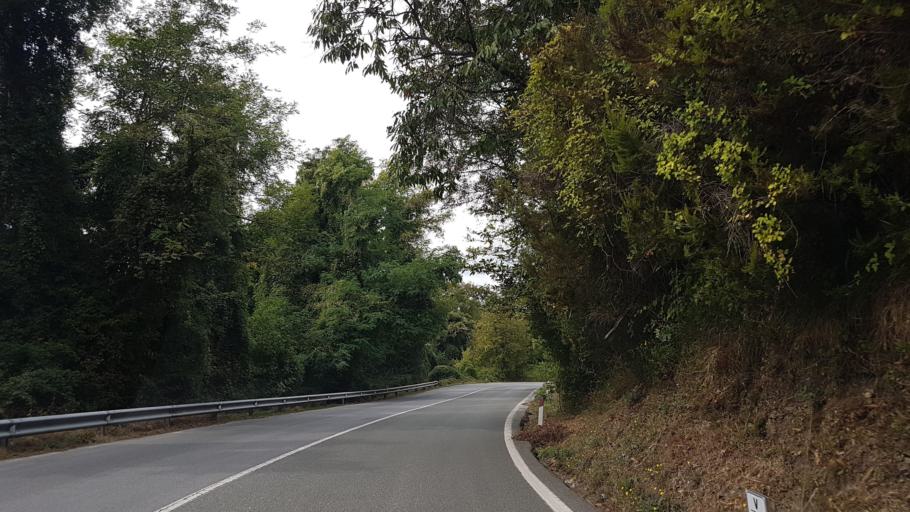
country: IT
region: Liguria
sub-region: Provincia di Genova
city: Castiglione
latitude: 44.2558
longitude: 9.5257
